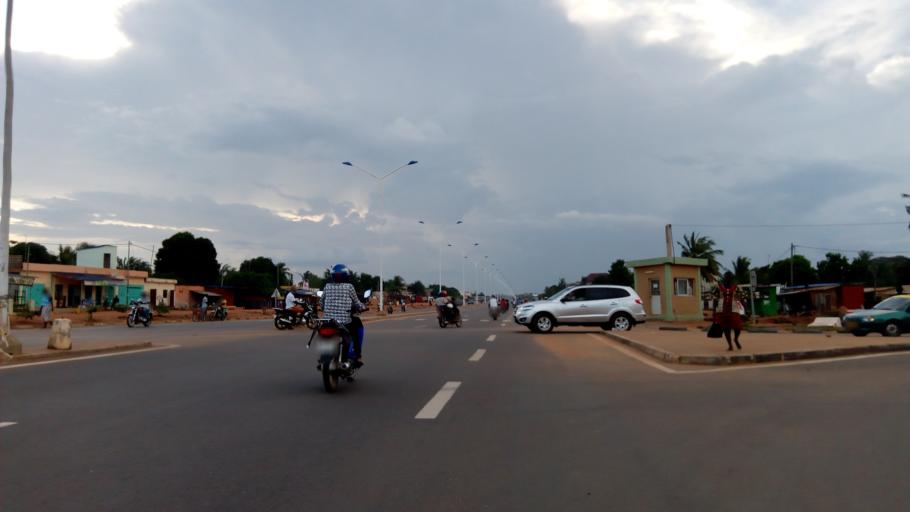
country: TG
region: Maritime
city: Lome
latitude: 6.2410
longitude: 1.2046
